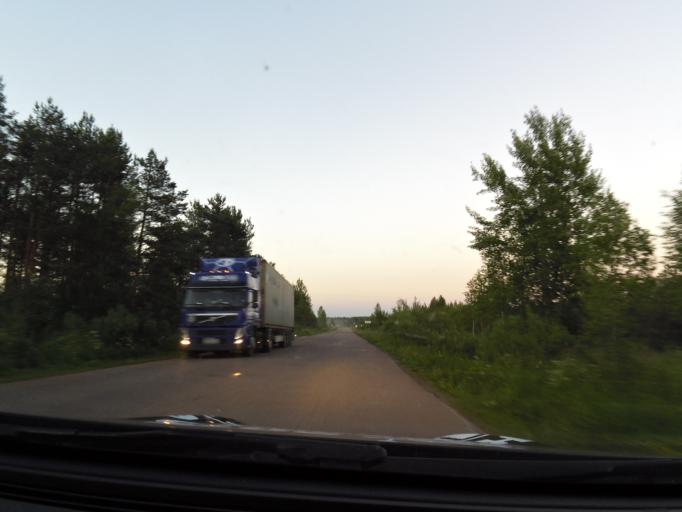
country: RU
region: Vologda
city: Vytegra
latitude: 60.8672
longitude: 35.9860
